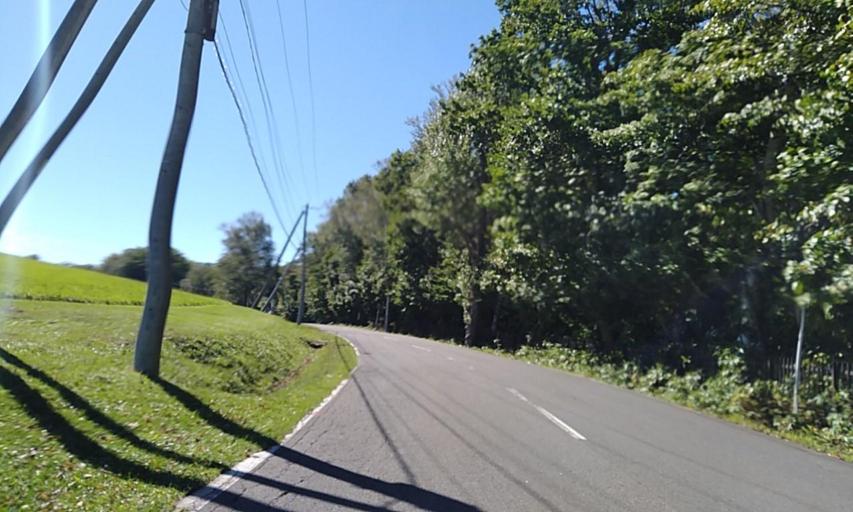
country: JP
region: Hokkaido
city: Sapporo
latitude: 43.0015
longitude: 141.3928
